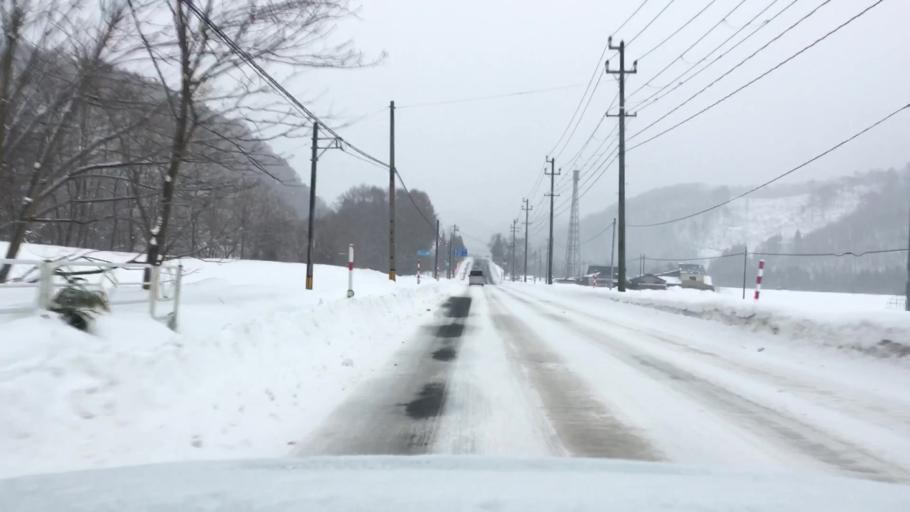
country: JP
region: Akita
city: Hanawa
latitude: 40.0592
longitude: 141.0121
